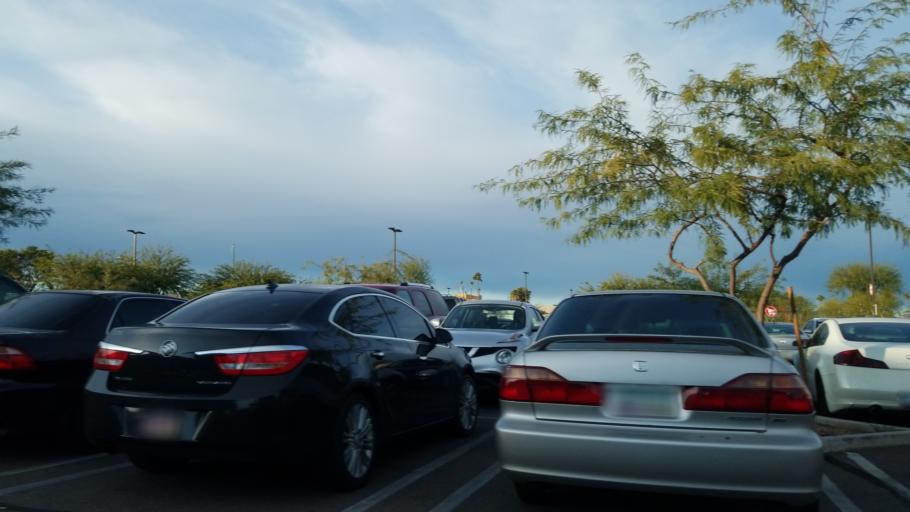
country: US
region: Arizona
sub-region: Maricopa County
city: Phoenix
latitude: 33.5205
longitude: -112.0989
